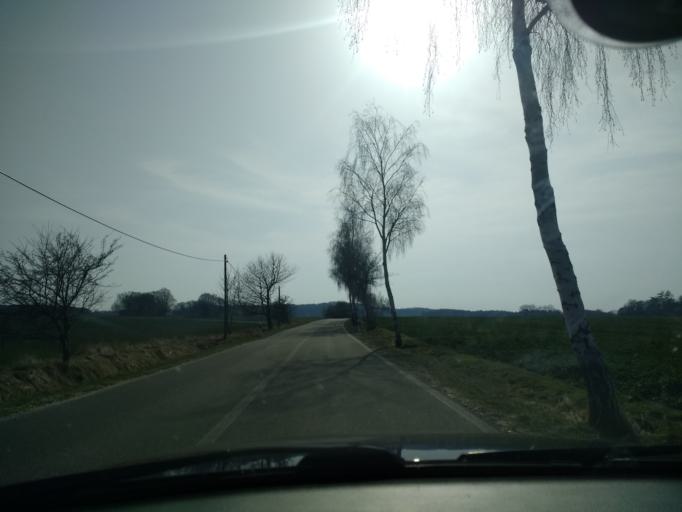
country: DE
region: Mecklenburg-Vorpommern
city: Bergen auf Ruegen
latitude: 54.4383
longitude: 13.4701
